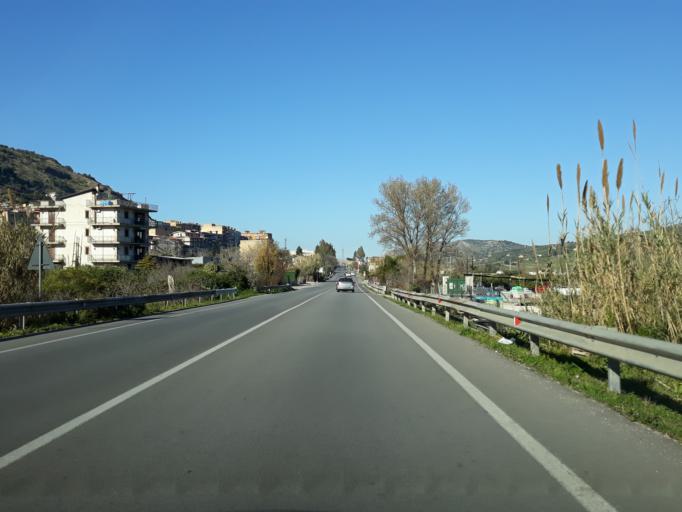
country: IT
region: Sicily
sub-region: Palermo
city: Misilmeri
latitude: 38.0300
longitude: 13.4563
